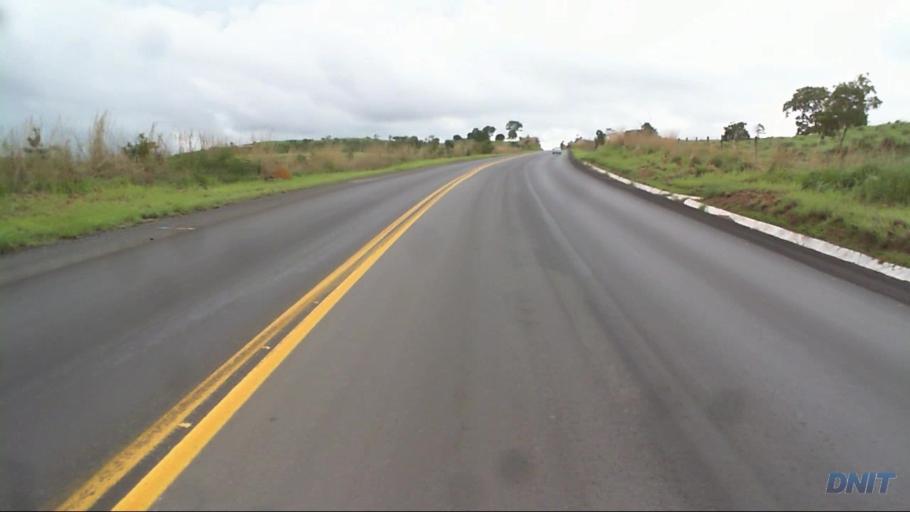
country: BR
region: Goias
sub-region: Padre Bernardo
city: Padre Bernardo
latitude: -15.2198
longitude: -48.5295
